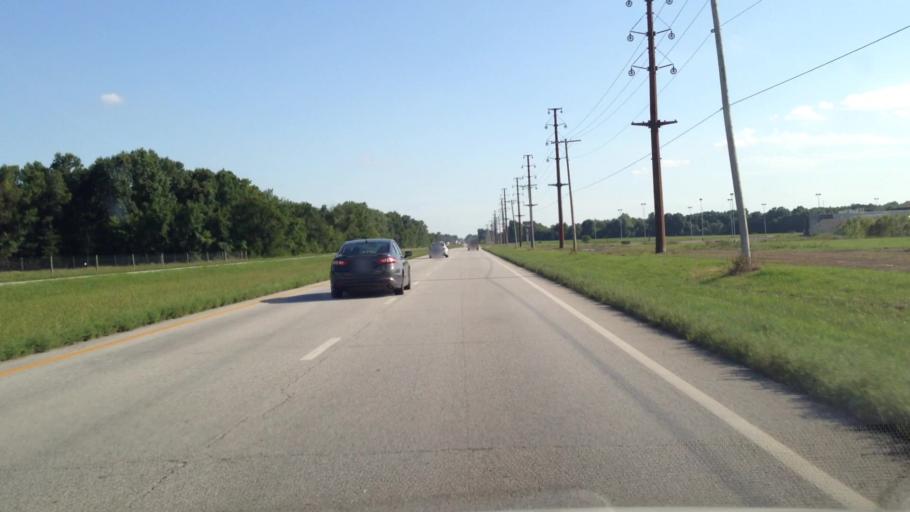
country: US
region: Kansas
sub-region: Crawford County
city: Frontenac
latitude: 37.4818
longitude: -94.7053
